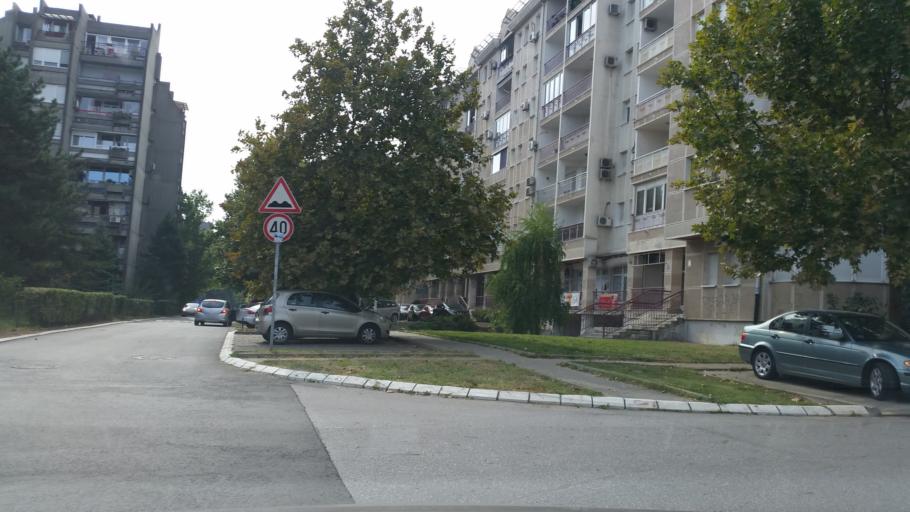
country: RS
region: Central Serbia
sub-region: Belgrade
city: Novi Beograd
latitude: 44.8128
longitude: 20.4279
